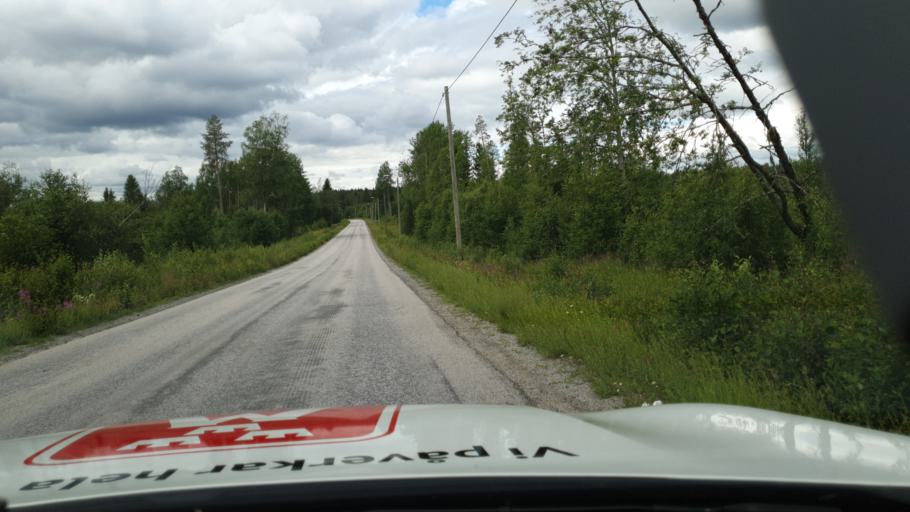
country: SE
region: Vaesterbotten
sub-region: Nordmalings Kommun
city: Nordmaling
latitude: 63.5814
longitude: 19.4805
